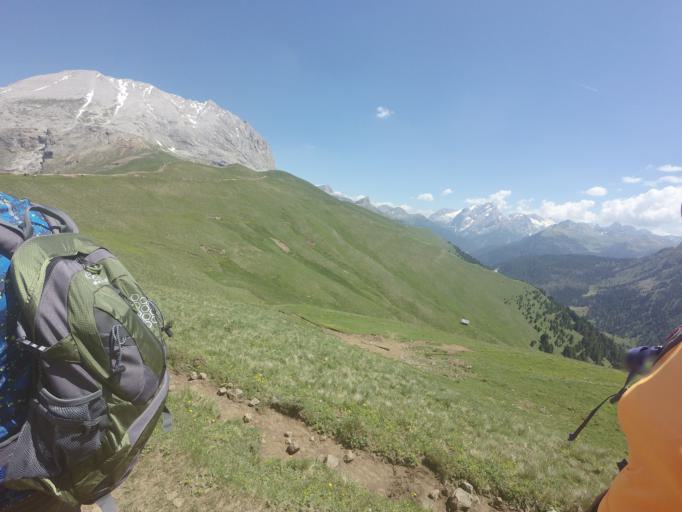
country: IT
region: Trentino-Alto Adige
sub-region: Provincia di Trento
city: Mazzin
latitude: 46.5021
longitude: 11.6883
